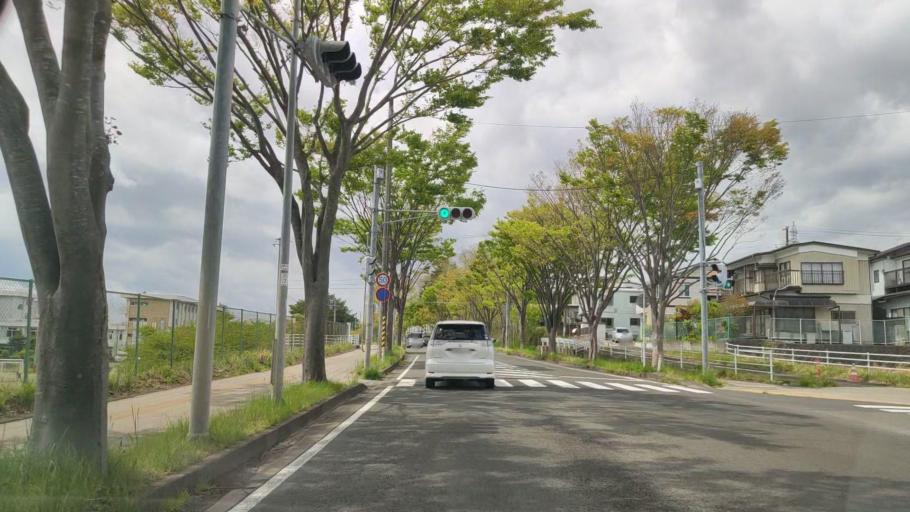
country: JP
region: Miyagi
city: Shiogama
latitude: 38.3032
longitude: 141.0284
